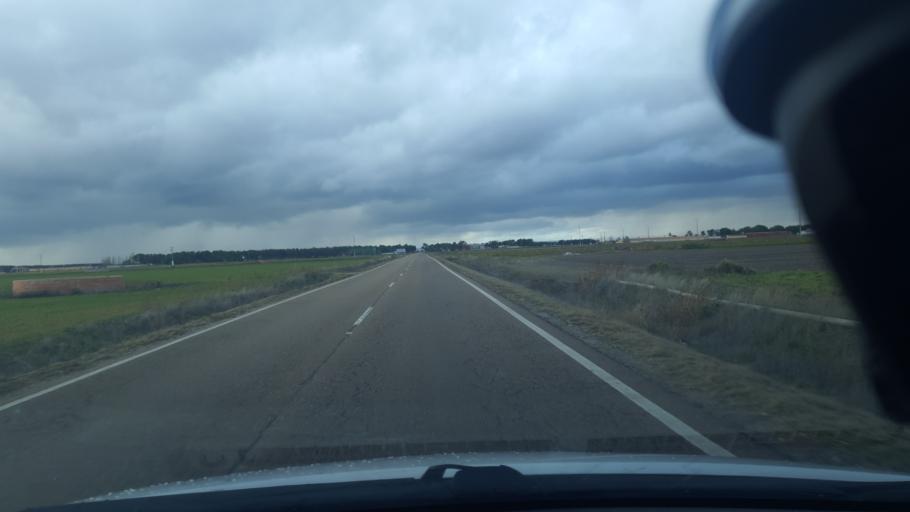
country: ES
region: Castille and Leon
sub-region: Provincia de Segovia
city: Sanchonuno
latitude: 41.2953
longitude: -4.3347
